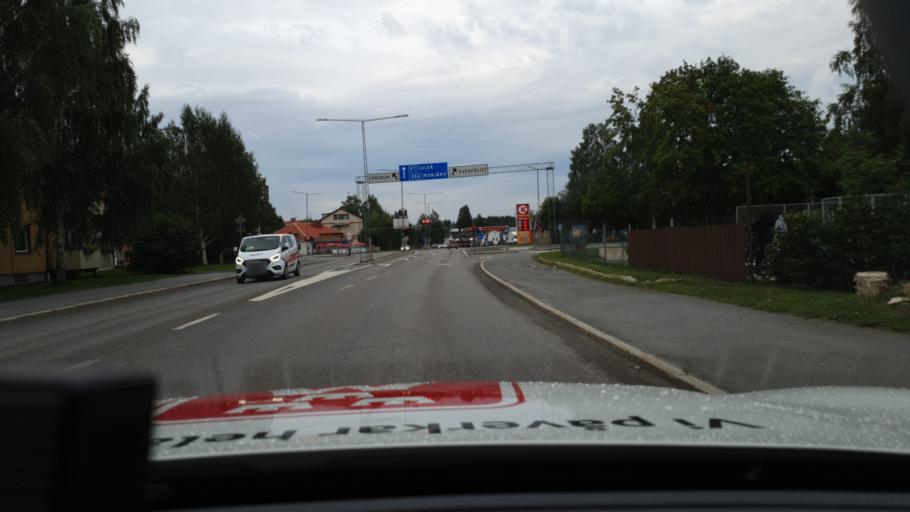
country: SE
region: Norrbotten
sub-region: Bodens Kommun
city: Boden
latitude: 65.8223
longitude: 21.6774
